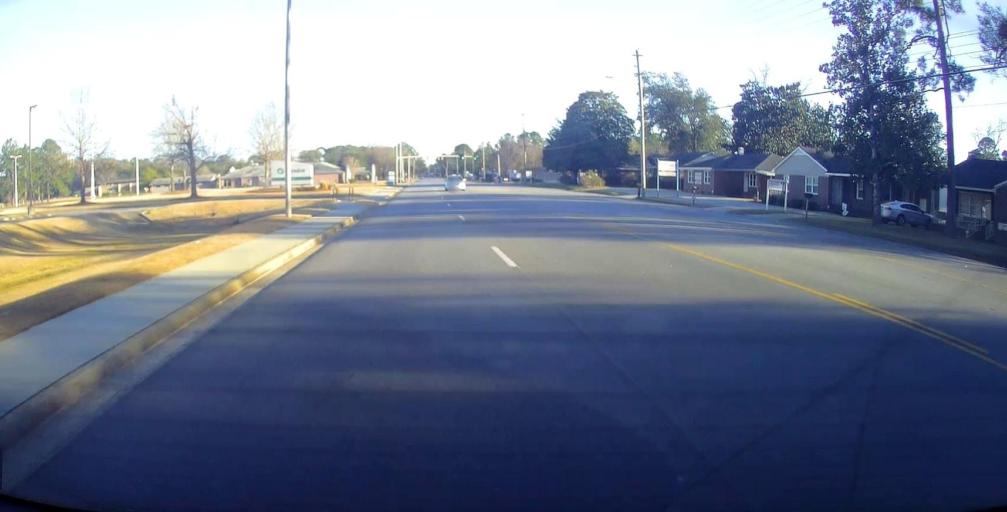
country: US
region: Georgia
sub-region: Dougherty County
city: Albany
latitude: 31.6061
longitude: -84.1717
